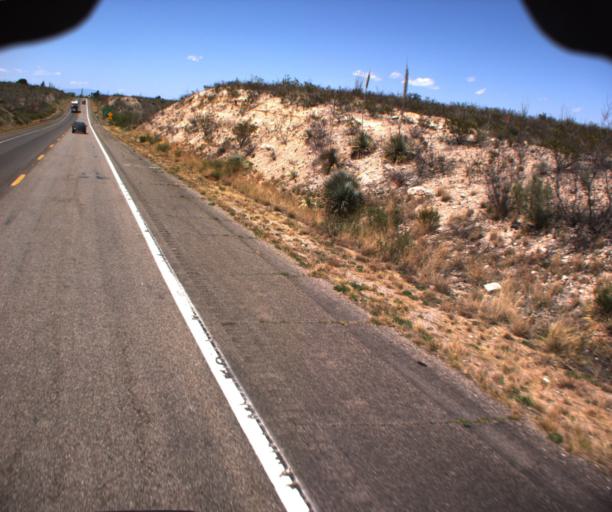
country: US
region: Arizona
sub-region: Cochise County
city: Tombstone
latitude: 31.7022
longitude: -110.0491
